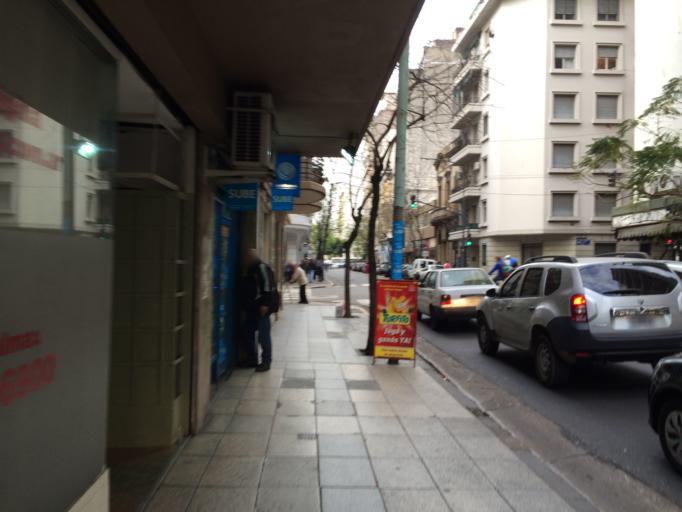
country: AR
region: Buenos Aires F.D.
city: Buenos Aires
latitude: -34.6113
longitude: -58.4017
